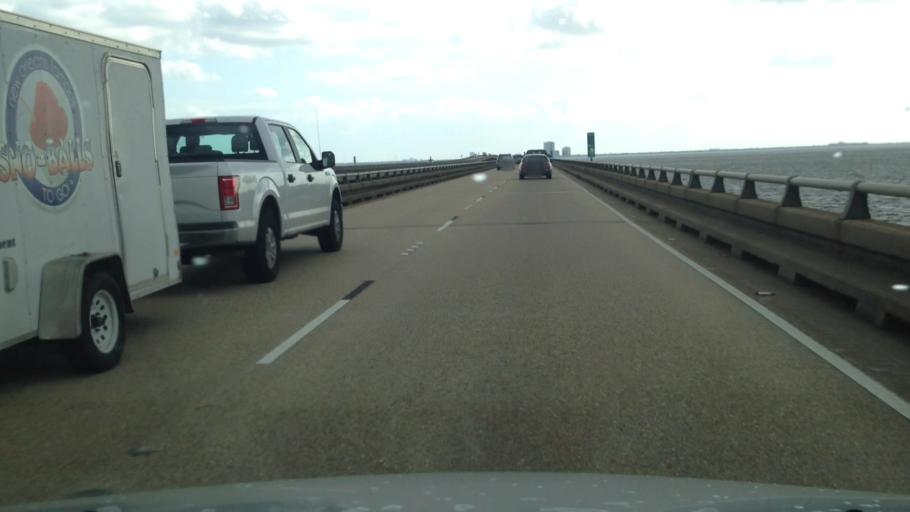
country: US
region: Louisiana
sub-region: Jefferson Parish
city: Metairie
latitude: 30.0840
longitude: -90.1432
